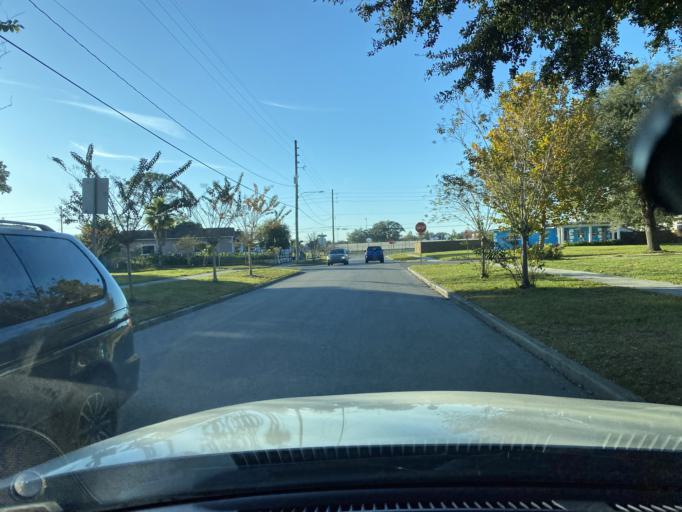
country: US
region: Florida
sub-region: Orange County
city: Azalea Park
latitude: 28.5328
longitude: -81.3019
